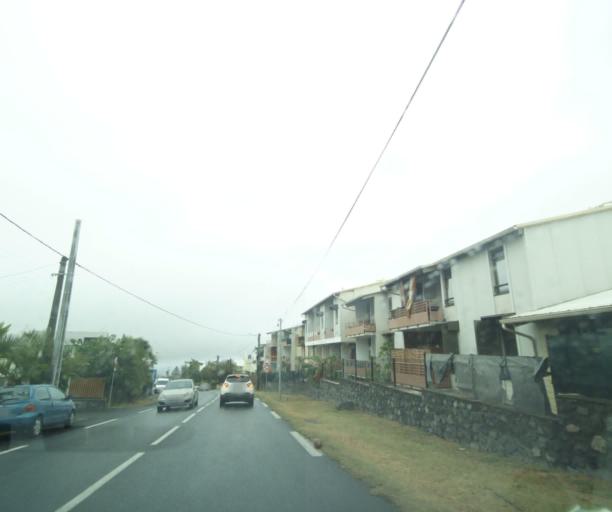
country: RE
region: Reunion
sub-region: Reunion
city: Saint-Paul
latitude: -21.0436
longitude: 55.2574
